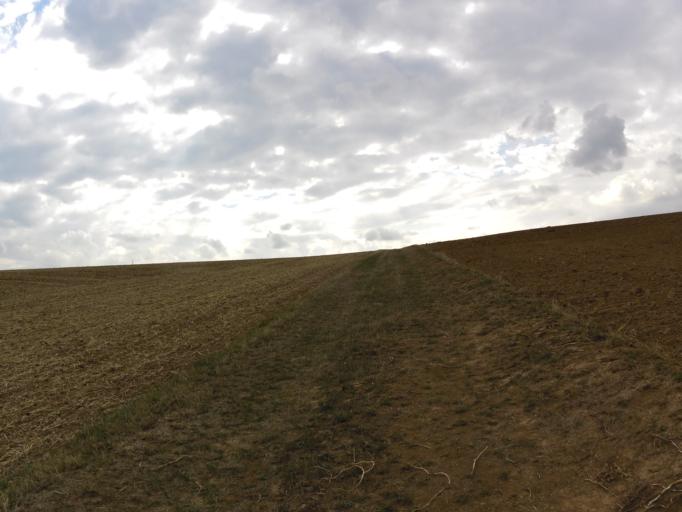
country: DE
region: Bavaria
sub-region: Regierungsbezirk Unterfranken
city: Waldbrunn
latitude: 49.7673
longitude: 9.8160
